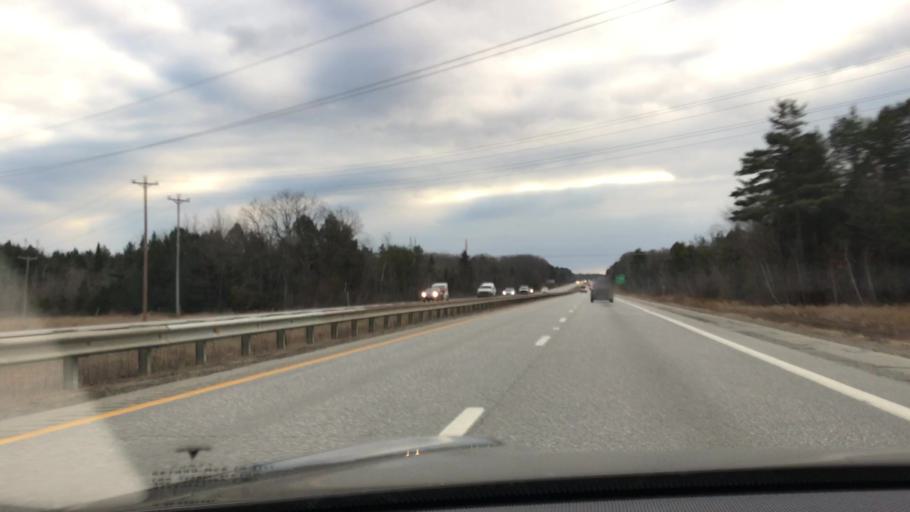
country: US
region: Maine
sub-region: Kennebec County
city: Hallowell
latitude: 44.2572
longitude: -69.8072
